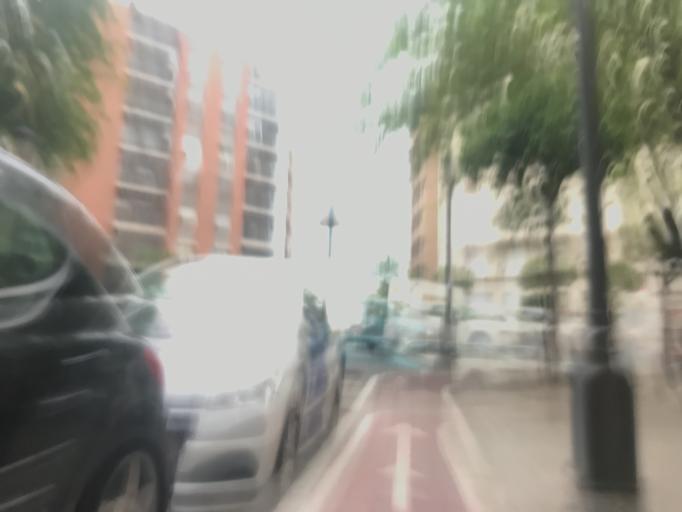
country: ES
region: Valencia
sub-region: Provincia de Valencia
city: Valencia
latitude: 39.4627
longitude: -0.3811
